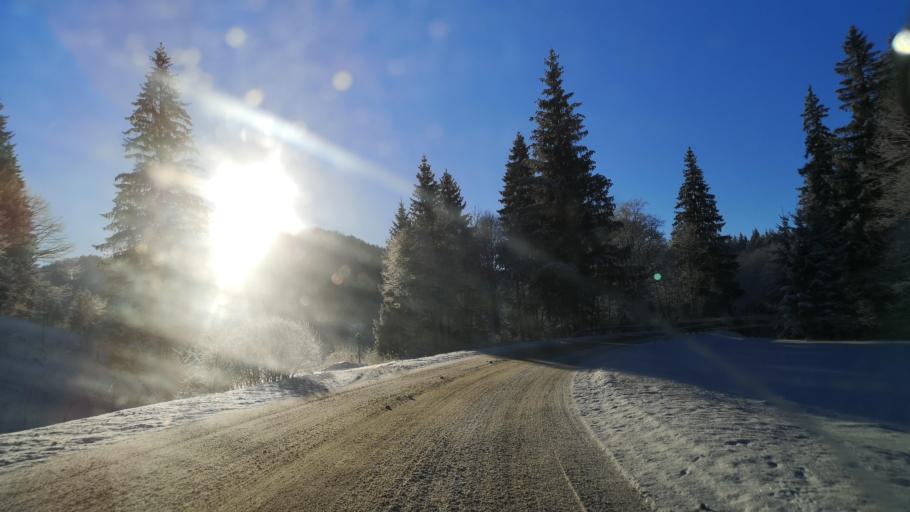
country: SK
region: Banskobystricky
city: Revuca
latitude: 48.8378
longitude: 20.0462
